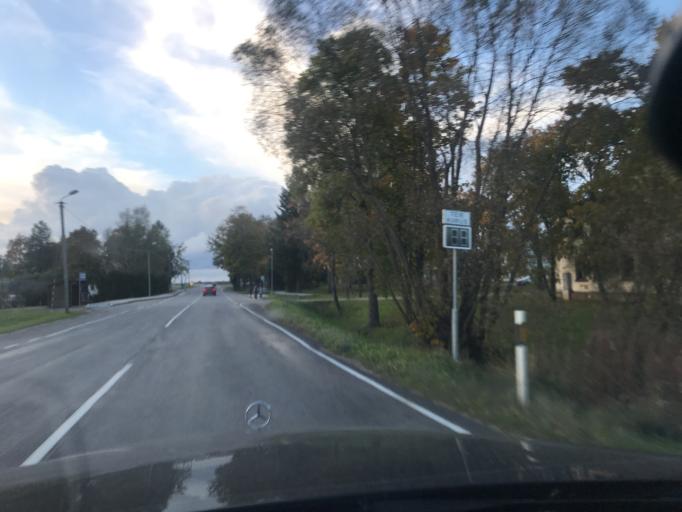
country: EE
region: Vorumaa
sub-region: Antsla vald
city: Vana-Antsla
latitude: 57.8919
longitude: 26.5025
